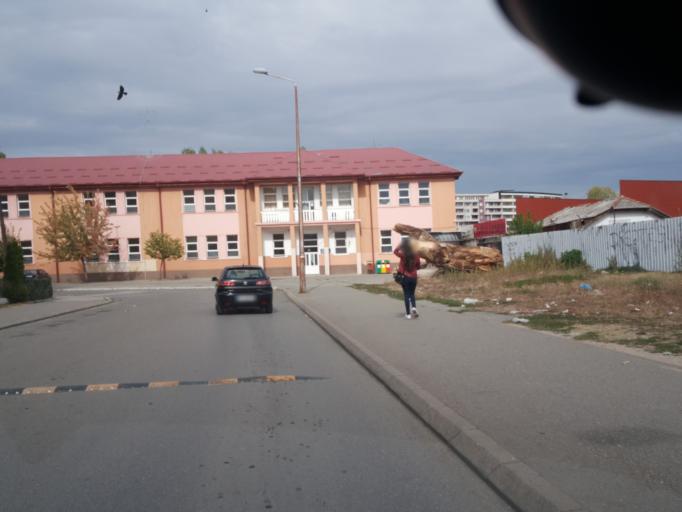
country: XK
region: Gjakova
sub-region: Komuna e Gjakoves
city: Gjakove
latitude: 42.3839
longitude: 20.4336
